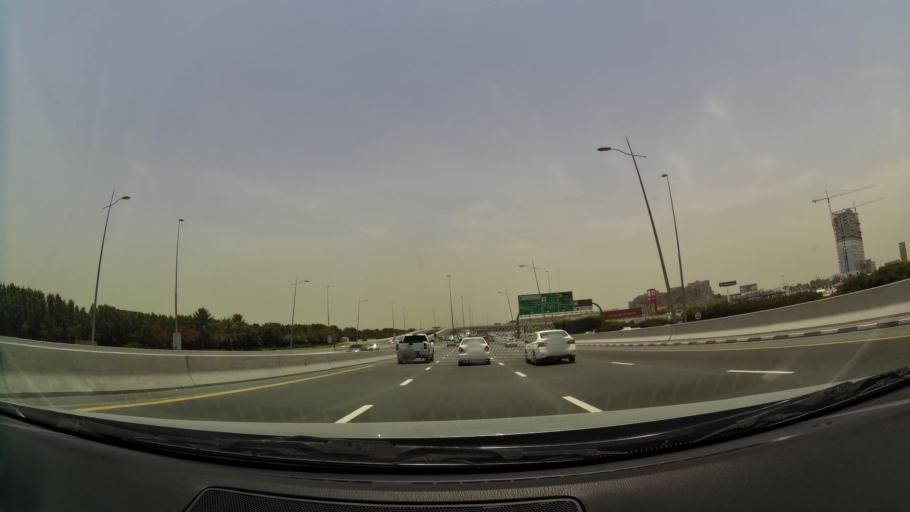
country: AE
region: Ash Shariqah
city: Sharjah
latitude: 25.2268
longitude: 55.3565
